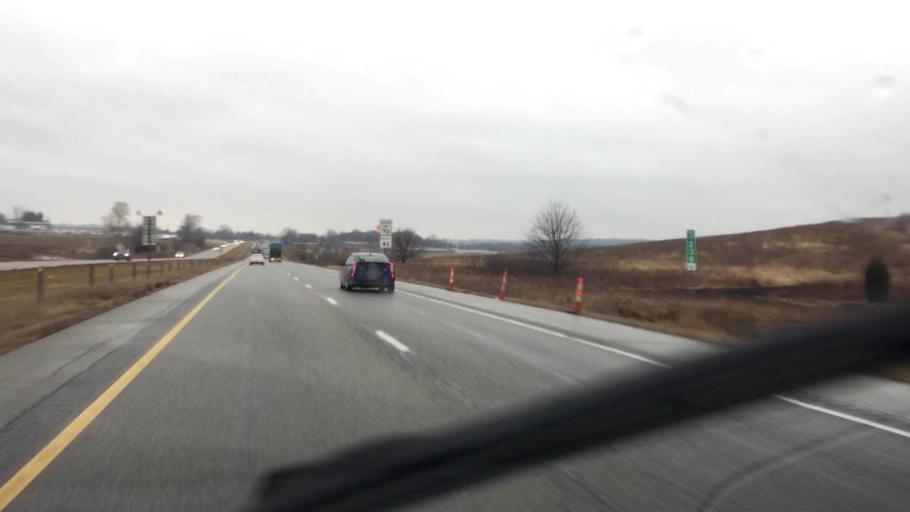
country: US
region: Iowa
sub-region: Johnson County
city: Tiffin
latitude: 41.6943
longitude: -91.6478
